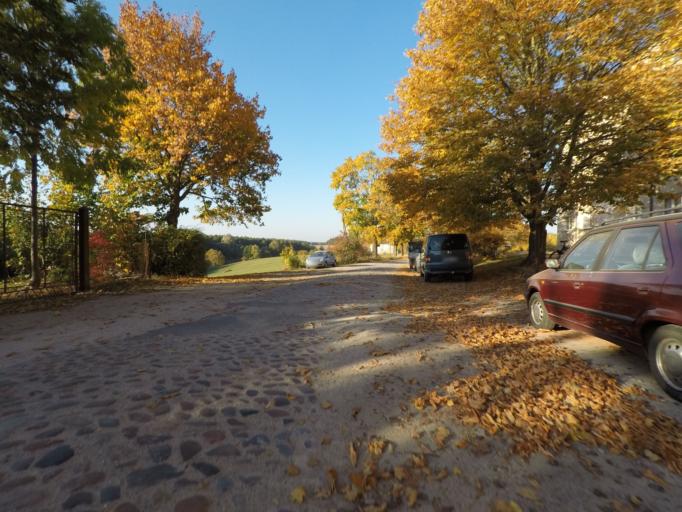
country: DE
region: Brandenburg
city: Biesenthal
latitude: 52.7676
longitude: 13.6375
